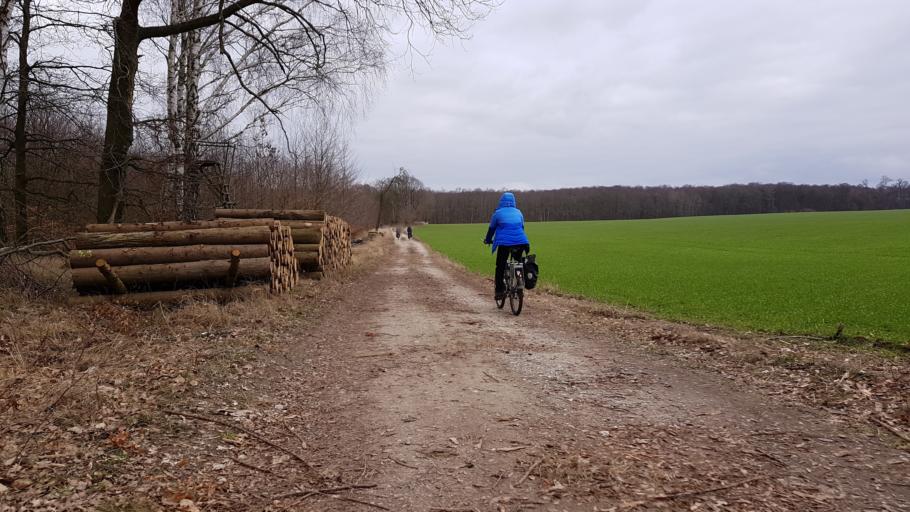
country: PL
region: West Pomeranian Voivodeship
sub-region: Powiat gryfinski
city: Banie
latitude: 53.0754
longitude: 14.7284
